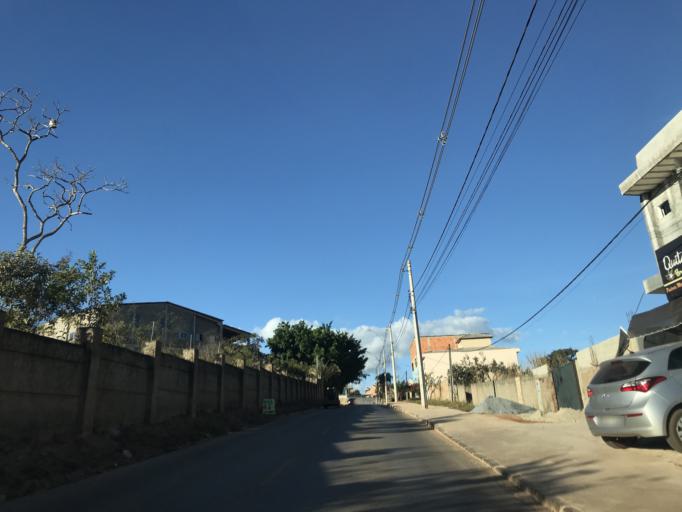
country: BR
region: Federal District
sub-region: Brasilia
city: Brasilia
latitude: -15.8833
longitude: -47.7693
